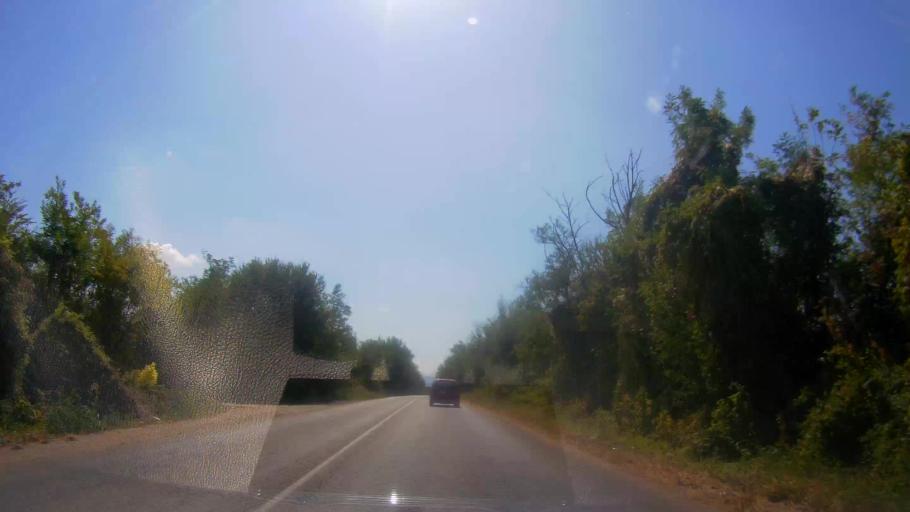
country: BG
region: Veliko Turnovo
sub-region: Obshtina Gorna Oryakhovitsa
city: Purvomaytsi
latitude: 43.2547
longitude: 25.6427
